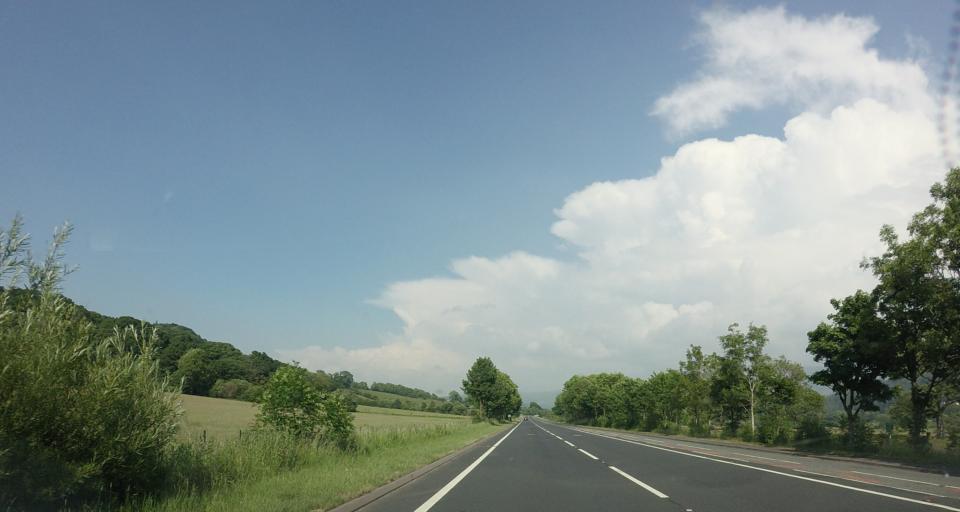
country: GB
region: England
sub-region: Cumbria
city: Cockermouth
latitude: 54.6655
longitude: -3.2640
